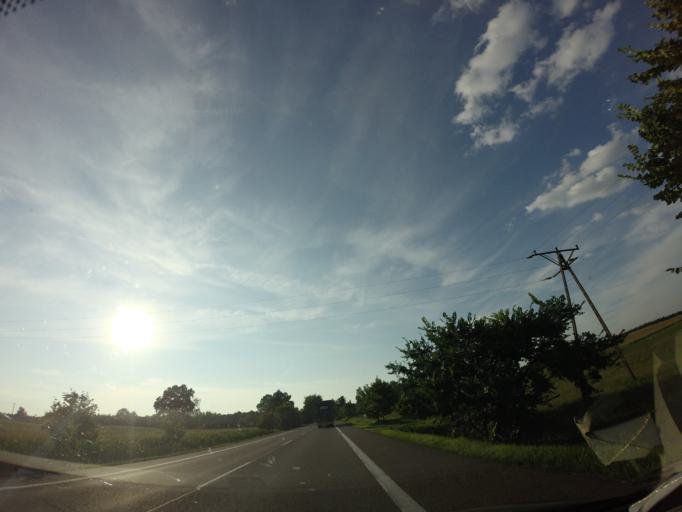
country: PL
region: Podlasie
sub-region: Powiat augustowski
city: Augustow
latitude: 53.7939
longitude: 22.9853
